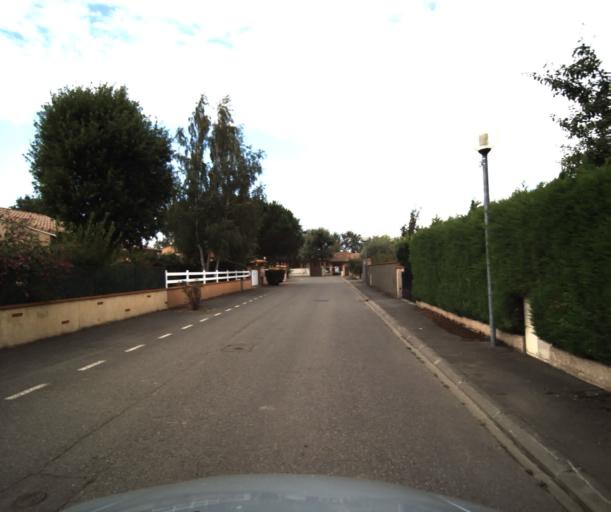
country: FR
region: Midi-Pyrenees
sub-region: Departement de la Haute-Garonne
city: Muret
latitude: 43.4448
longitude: 1.3197
